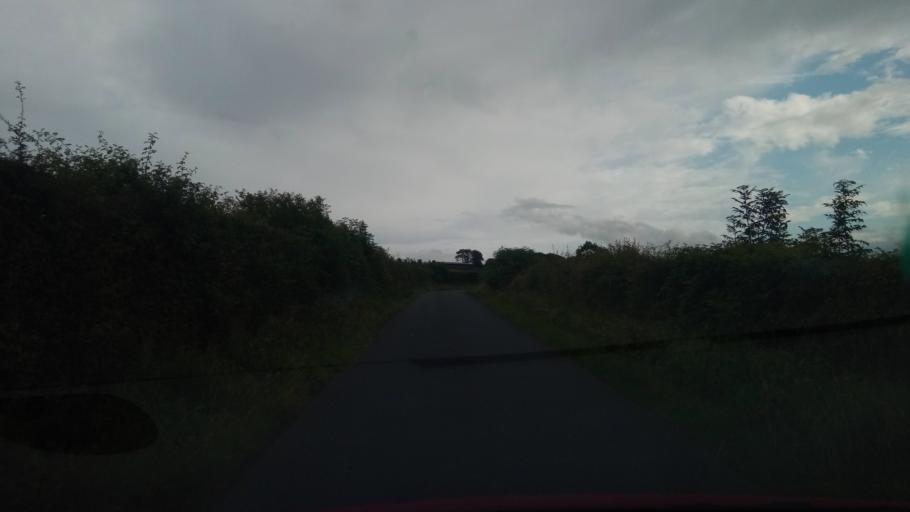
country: GB
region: Scotland
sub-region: The Scottish Borders
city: Hawick
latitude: 55.4473
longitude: -2.6858
